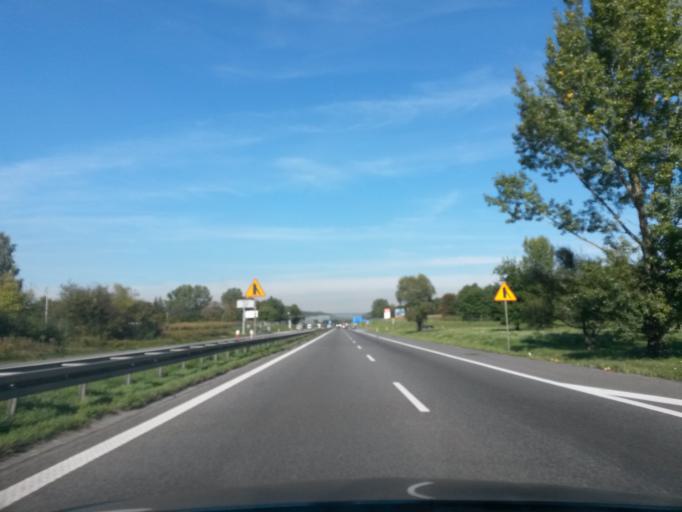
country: PL
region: Lesser Poland Voivodeship
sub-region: Powiat krakowski
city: Balice
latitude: 50.0742
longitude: 19.8098
